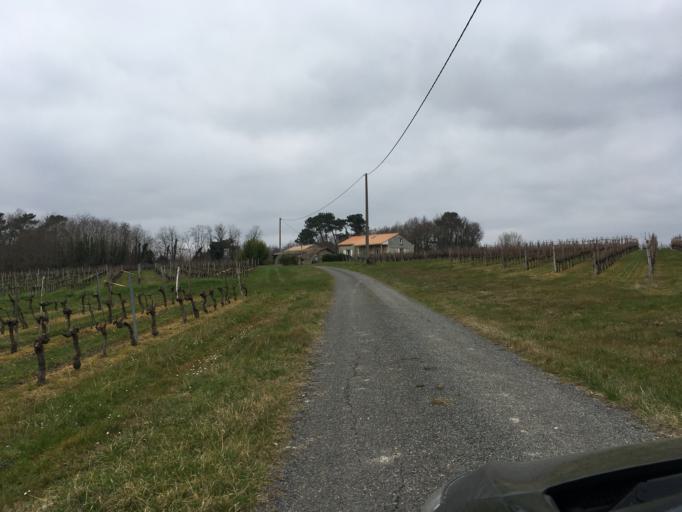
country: FR
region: Aquitaine
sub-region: Departement de la Gironde
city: Saint-Ciers-sur-Gironde
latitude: 45.3241
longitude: -0.5925
